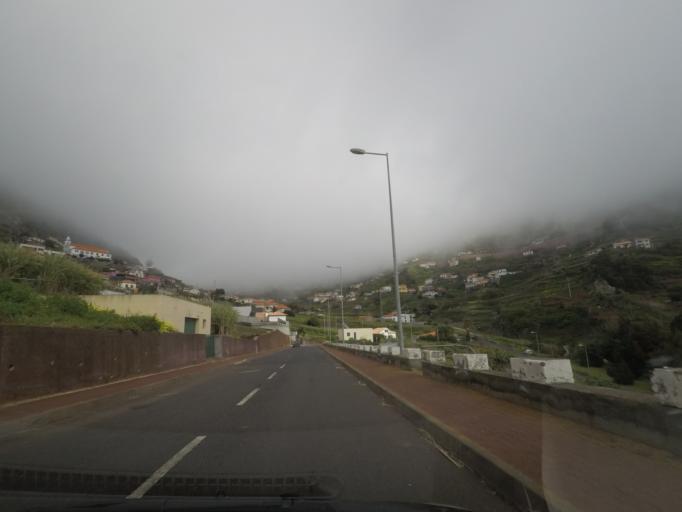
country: PT
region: Madeira
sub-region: Ribeira Brava
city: Campanario
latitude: 32.6599
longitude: -17.0130
